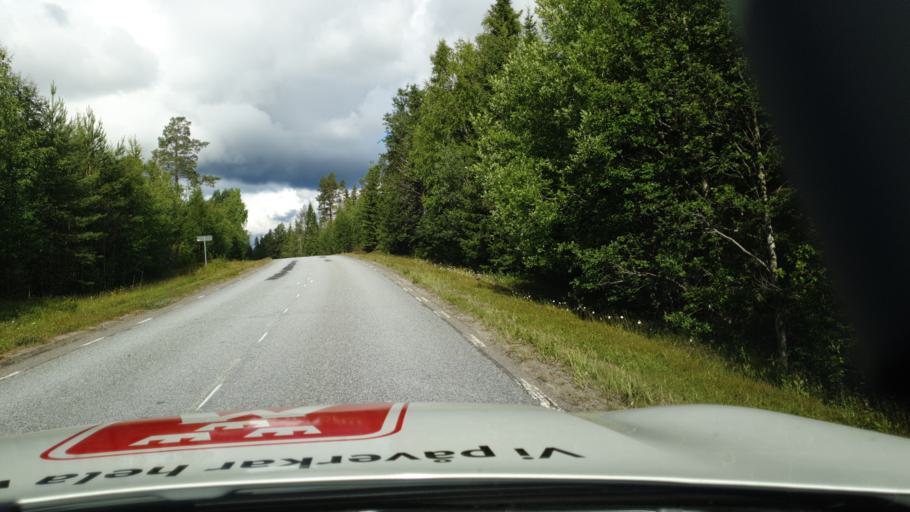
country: SE
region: Vaesterbotten
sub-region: Umea Kommun
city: Hoernefors
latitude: 63.6813
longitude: 20.0475
